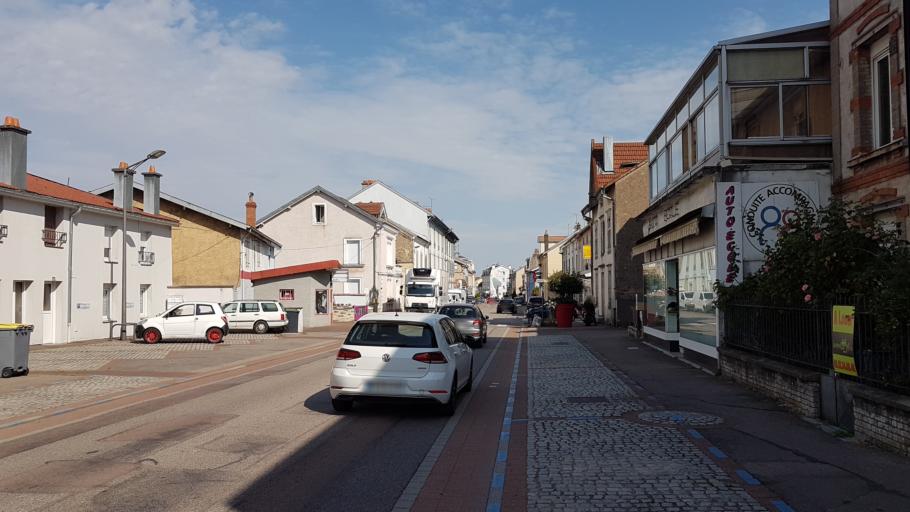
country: FR
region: Lorraine
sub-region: Departement des Vosges
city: Thaon-les-Vosges
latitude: 48.2484
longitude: 6.4225
